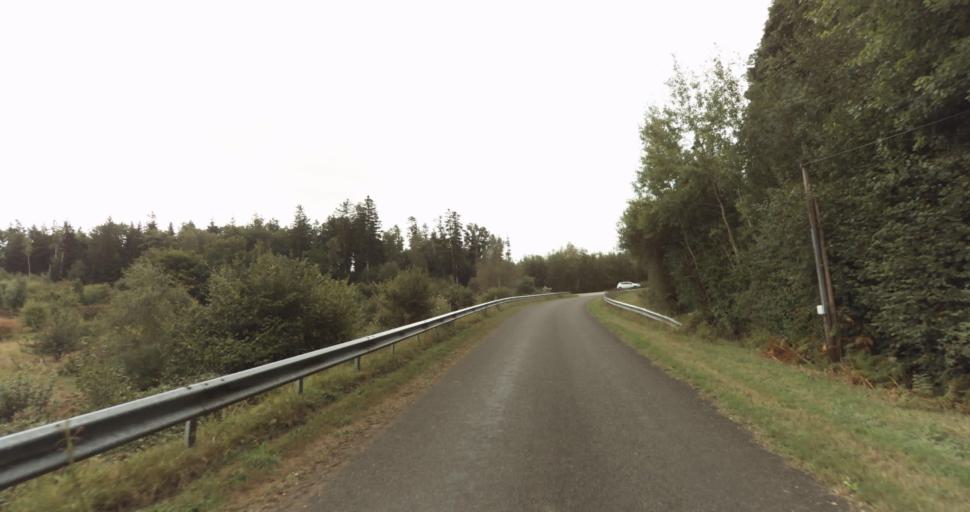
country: FR
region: Lower Normandy
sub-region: Departement de l'Orne
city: Gace
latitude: 48.7979
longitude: 0.3340
